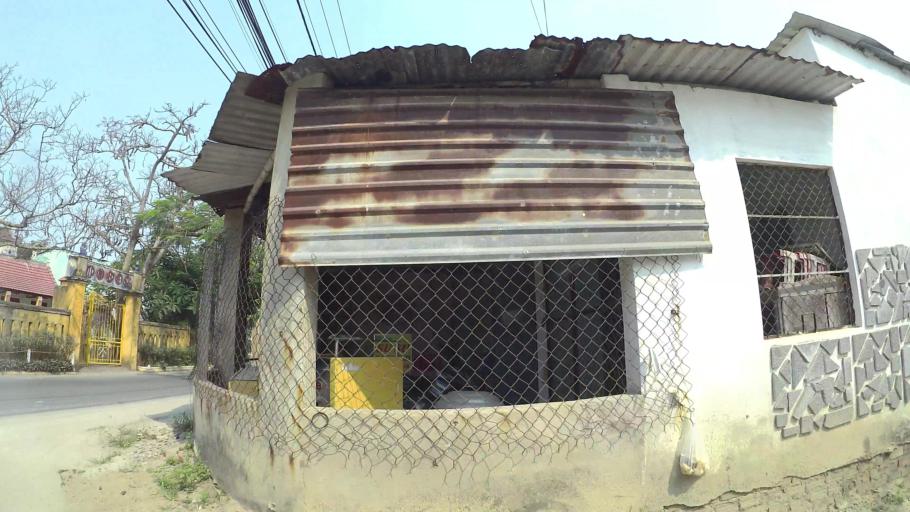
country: VN
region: Da Nang
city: Ngu Hanh Son
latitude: 15.9873
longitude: 108.2413
